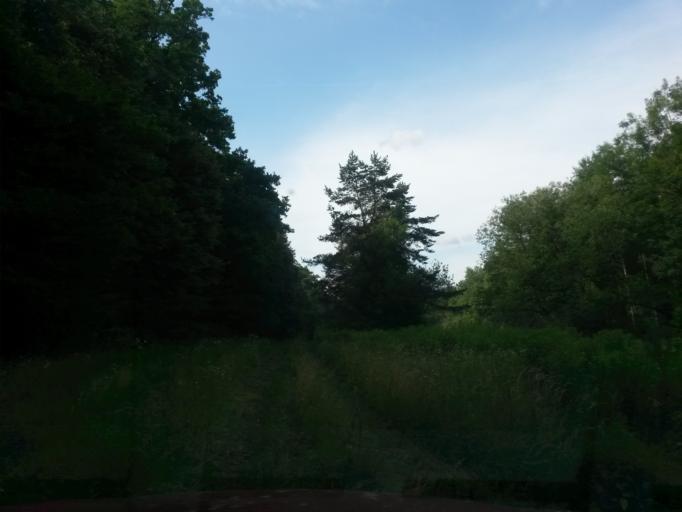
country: SK
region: Kosicky
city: Moldava nad Bodvou
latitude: 48.6165
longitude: 21.1124
